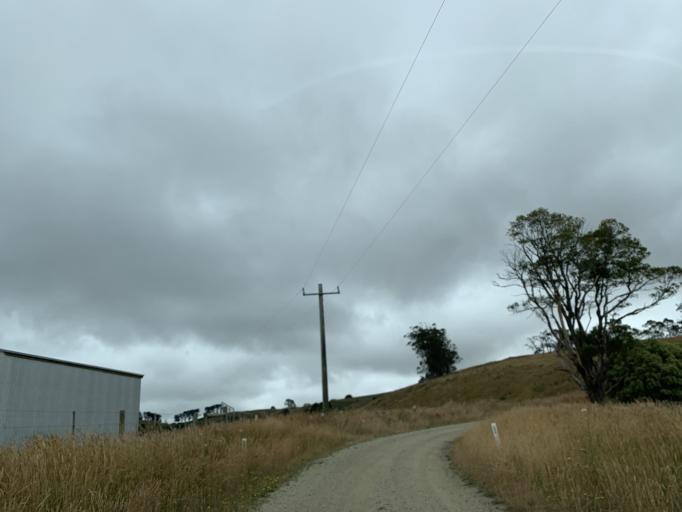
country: AU
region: Victoria
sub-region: Baw Baw
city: Warragul
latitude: -38.2962
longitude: 145.8895
